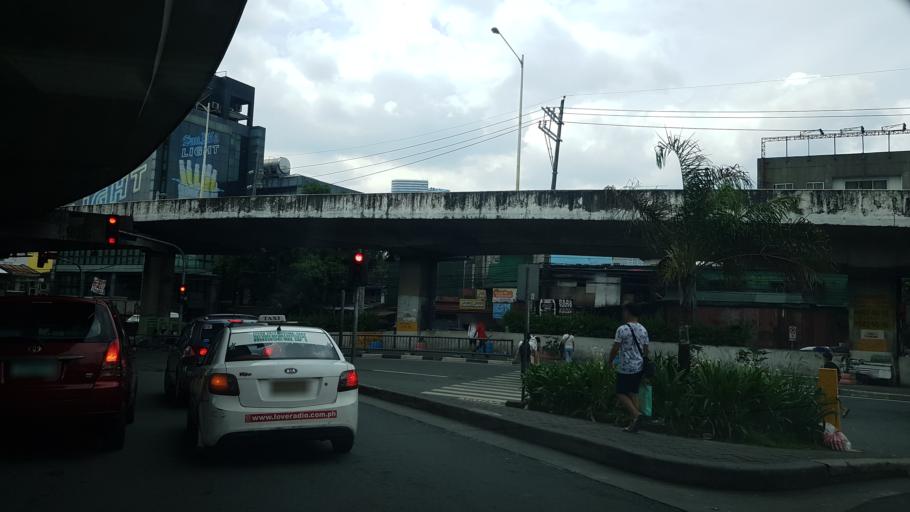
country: PH
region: Metro Manila
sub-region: Makati City
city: Makati City
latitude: 14.5571
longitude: 121.0424
